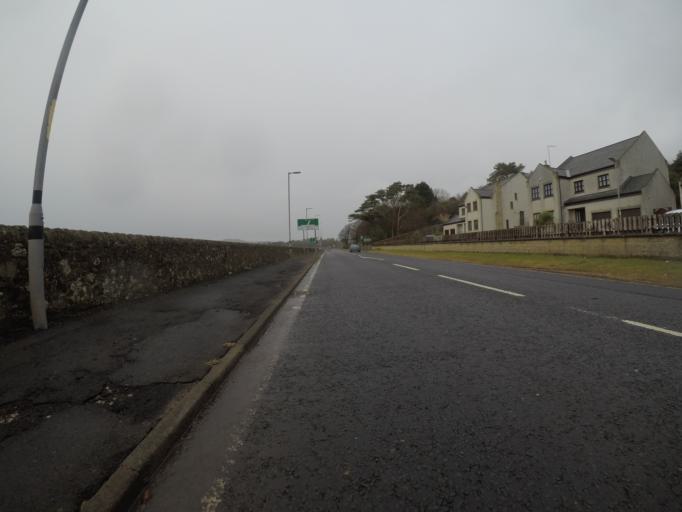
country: GB
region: Scotland
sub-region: North Ayrshire
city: West Kilbride
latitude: 55.6936
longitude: -4.8669
